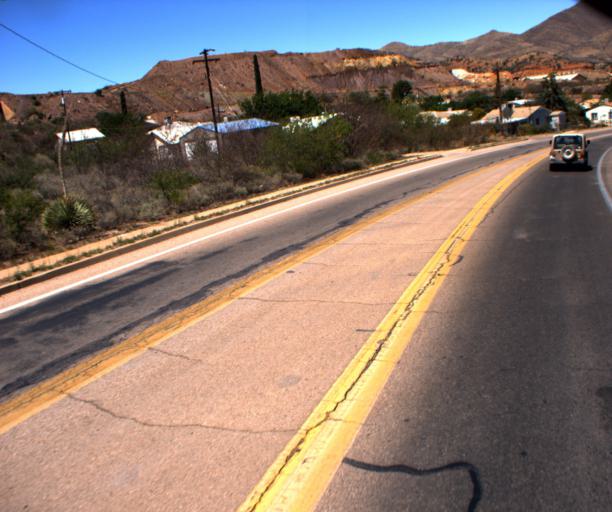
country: US
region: Arizona
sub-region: Cochise County
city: Bisbee
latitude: 31.4210
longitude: -109.8959
